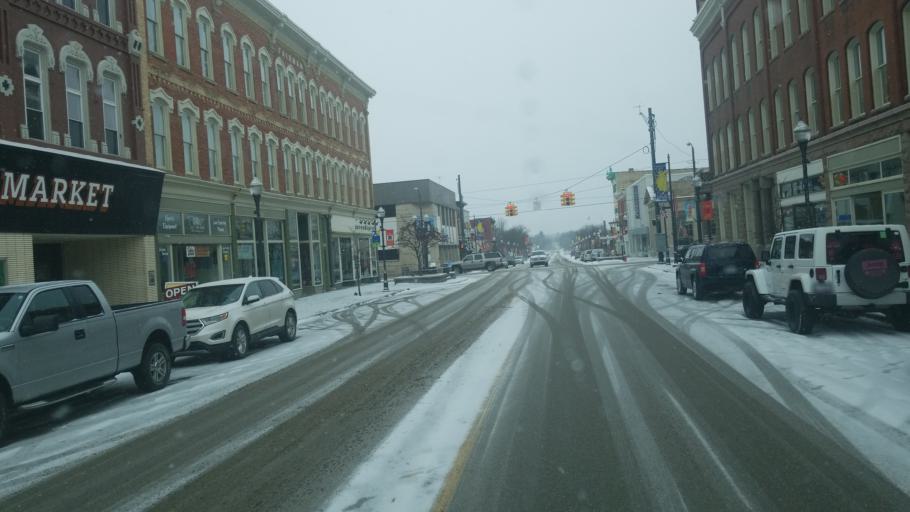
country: US
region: Michigan
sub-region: Mecosta County
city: Big Rapids
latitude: 43.6977
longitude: -85.4819
